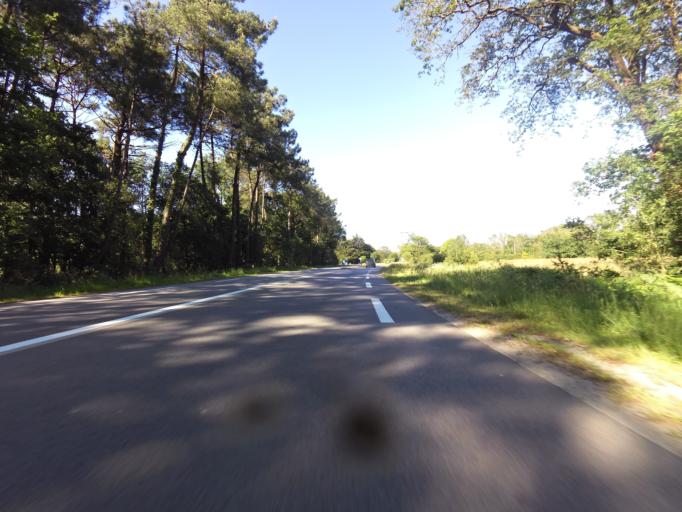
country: FR
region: Brittany
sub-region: Departement du Morbihan
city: Ferel
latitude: 47.5102
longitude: -2.3769
